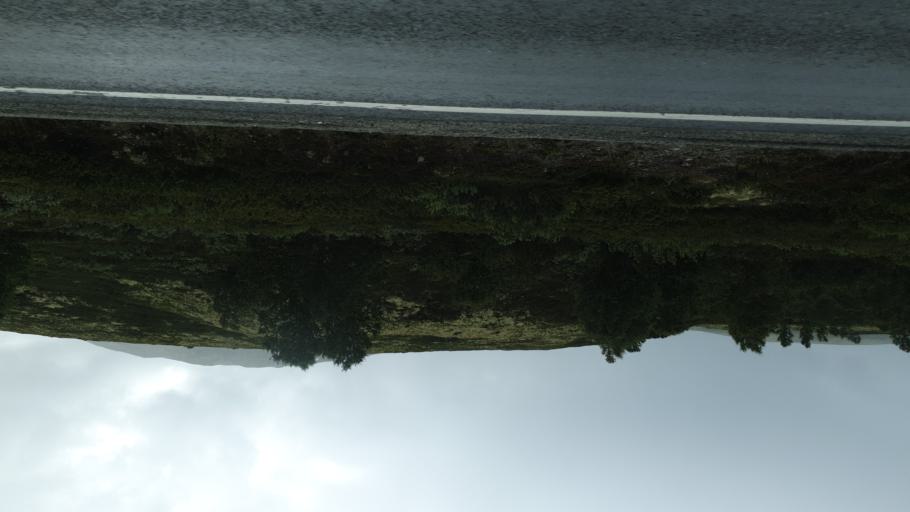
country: NO
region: Sor-Trondelag
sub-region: Oppdal
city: Oppdal
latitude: 62.2658
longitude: 9.5746
